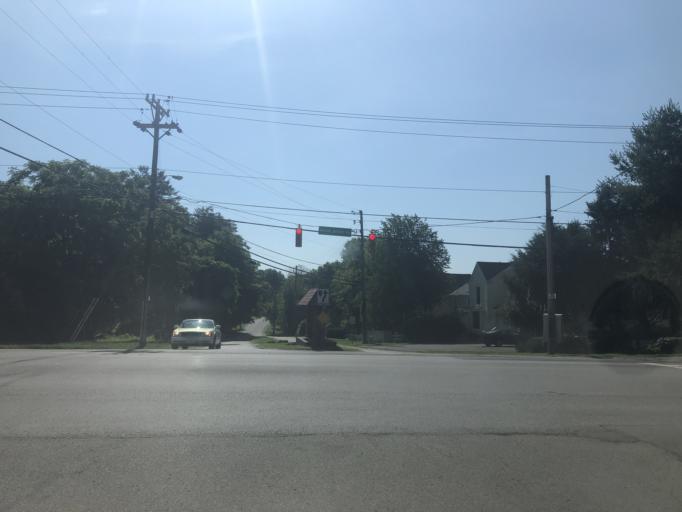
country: US
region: Tennessee
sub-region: Davidson County
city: Lakewood
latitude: 36.2069
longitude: -86.6058
